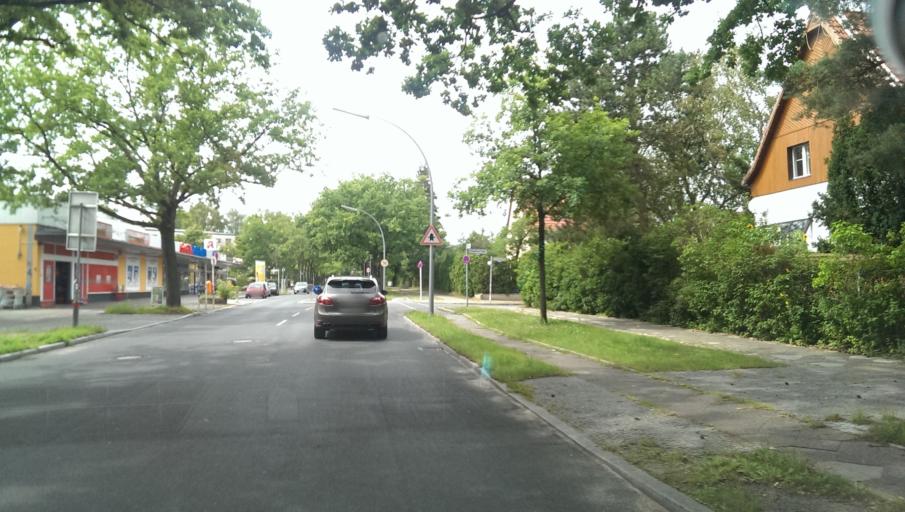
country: DE
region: Berlin
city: Zehlendorf Bezirk
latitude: 52.4231
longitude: 13.2431
